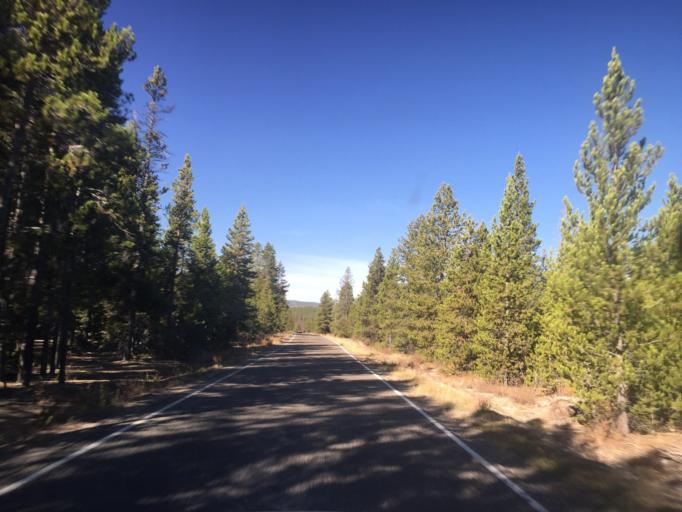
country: US
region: Montana
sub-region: Gallatin County
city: West Yellowstone
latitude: 44.5472
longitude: -110.7984
